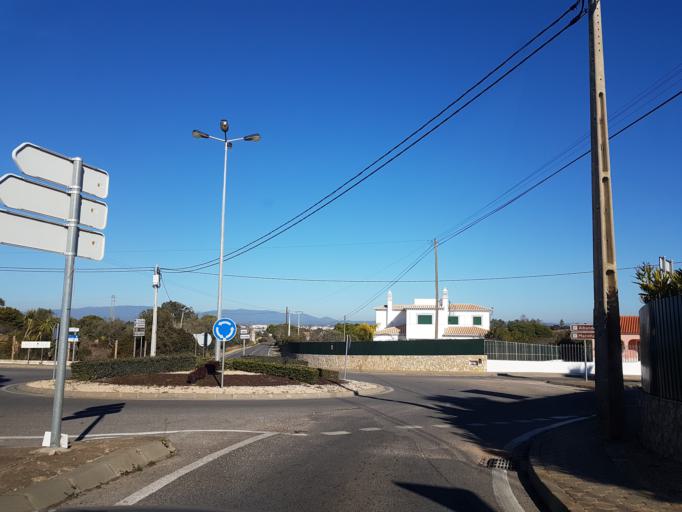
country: PT
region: Faro
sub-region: Lagoa
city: Carvoeiro
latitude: 37.1014
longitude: -8.4438
